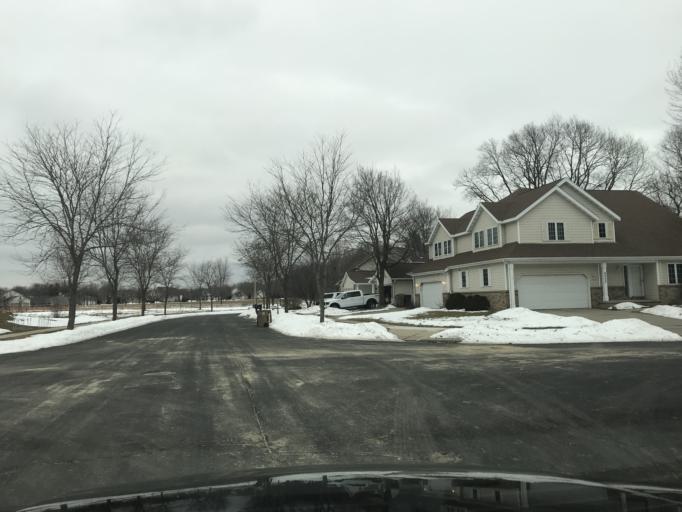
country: US
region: Wisconsin
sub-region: Dane County
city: Monona
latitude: 43.0770
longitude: -89.2722
